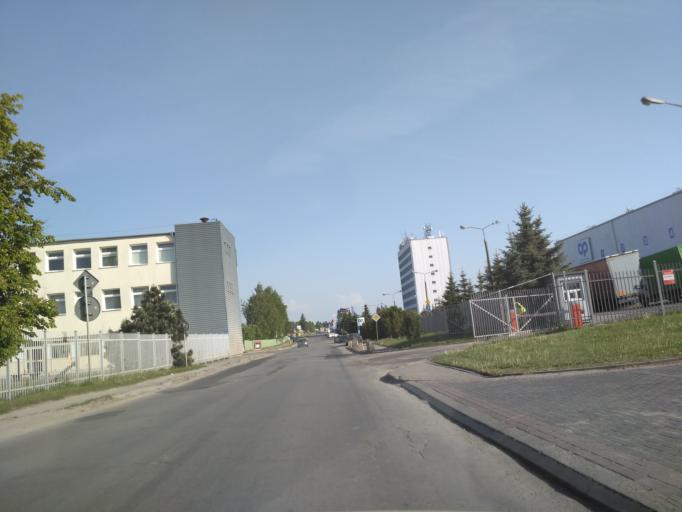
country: PL
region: Lublin Voivodeship
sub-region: Powiat lubelski
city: Lublin
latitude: 51.2113
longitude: 22.5593
